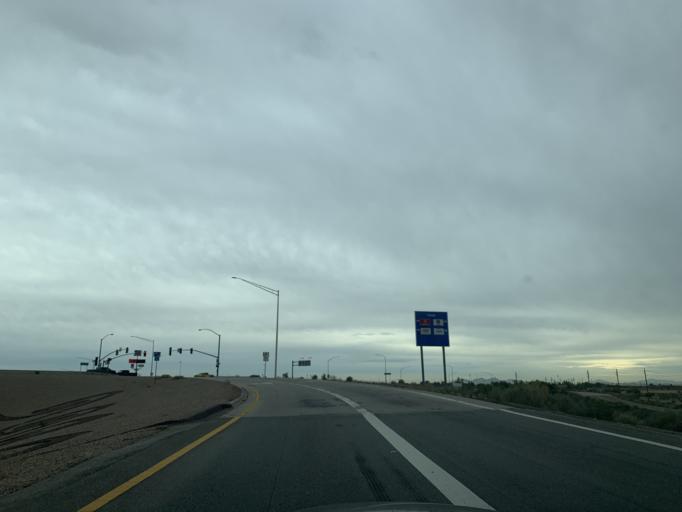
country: US
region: Arizona
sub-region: Pinal County
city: Arizona City
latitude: 32.7769
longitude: -111.6205
